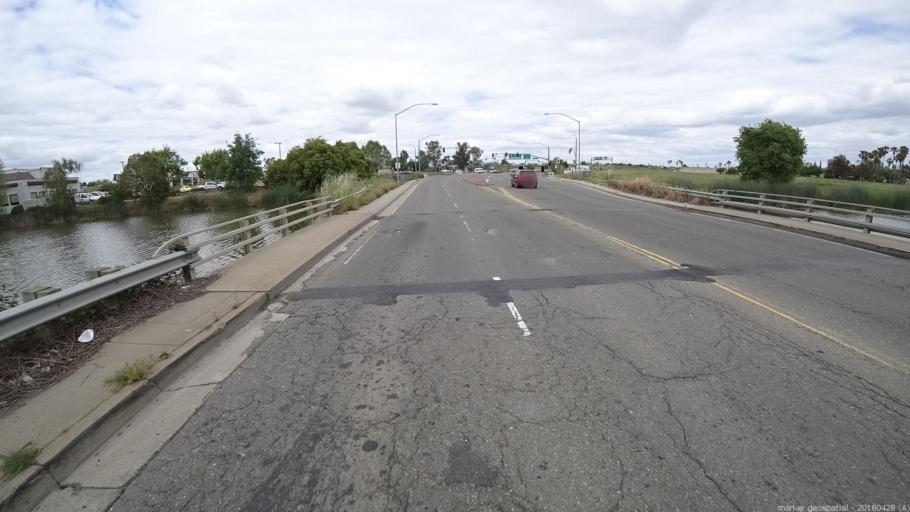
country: US
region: California
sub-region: Yolo County
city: West Sacramento
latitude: 38.5713
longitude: -121.5785
